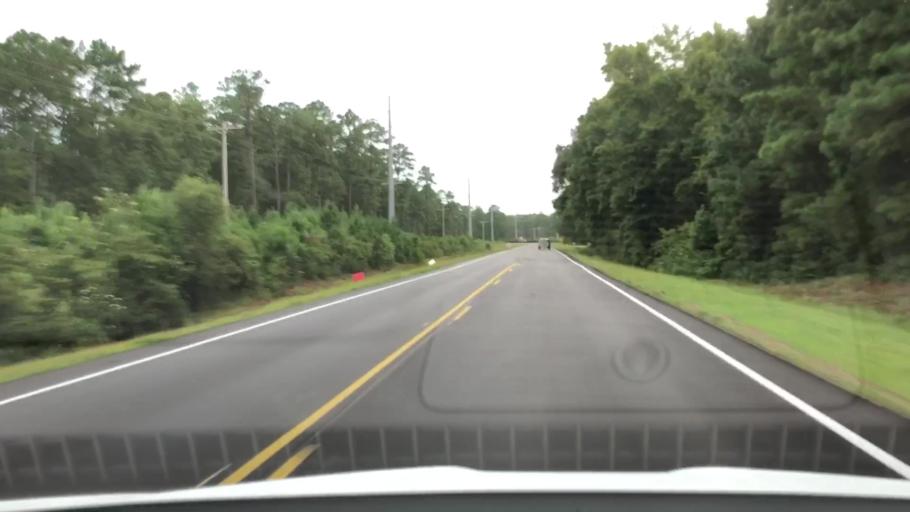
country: US
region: North Carolina
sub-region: Onslow County
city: Swansboro
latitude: 34.8038
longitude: -77.1325
